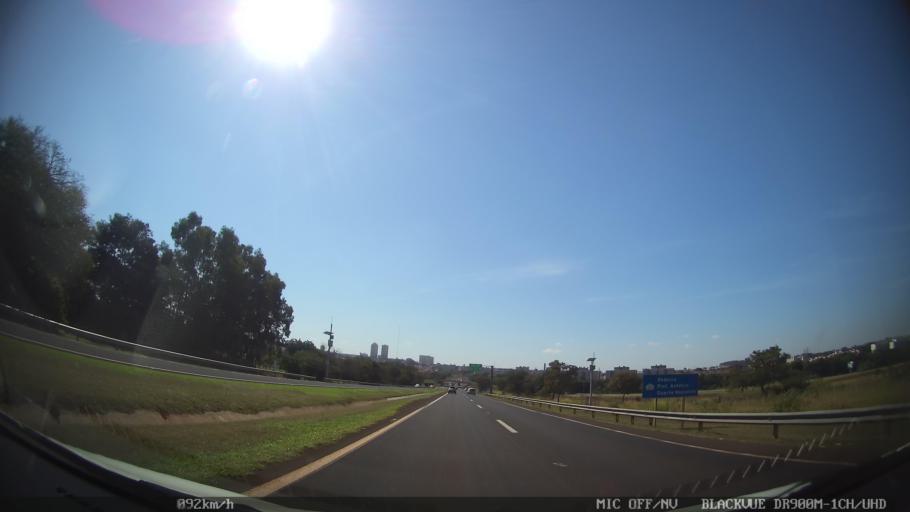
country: BR
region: Sao Paulo
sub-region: Ribeirao Preto
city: Ribeirao Preto
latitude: -21.2193
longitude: -47.7749
